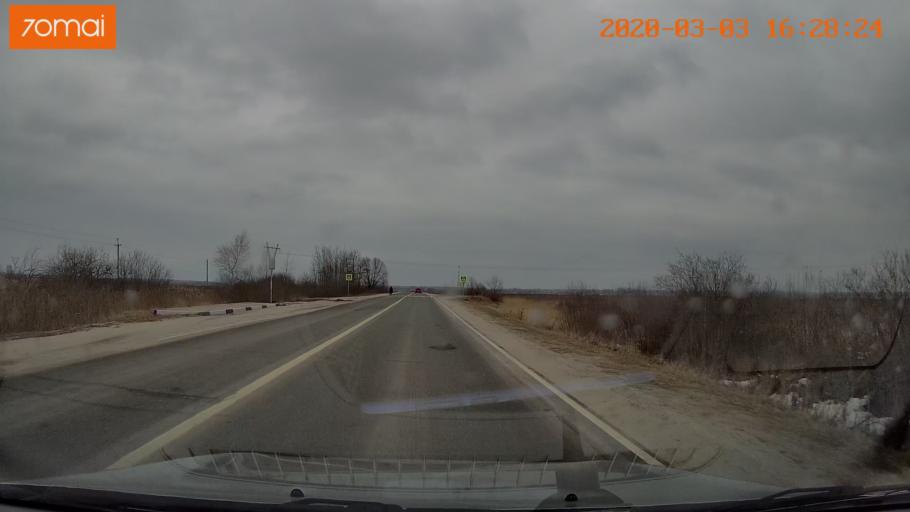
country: RU
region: Moskovskaya
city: Konobeyevo
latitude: 55.4381
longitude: 38.6847
